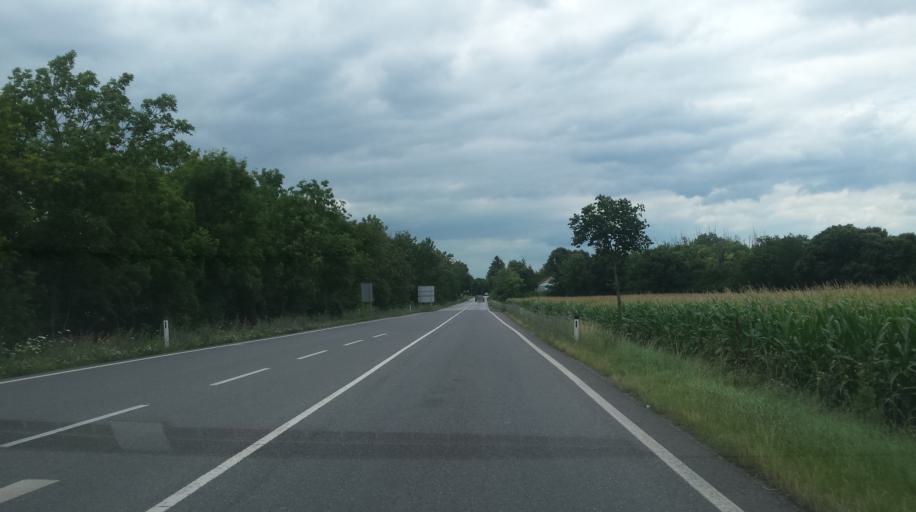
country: AT
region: Lower Austria
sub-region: Politischer Bezirk Wien-Umgebung
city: Himberg
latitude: 48.0635
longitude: 16.4571
